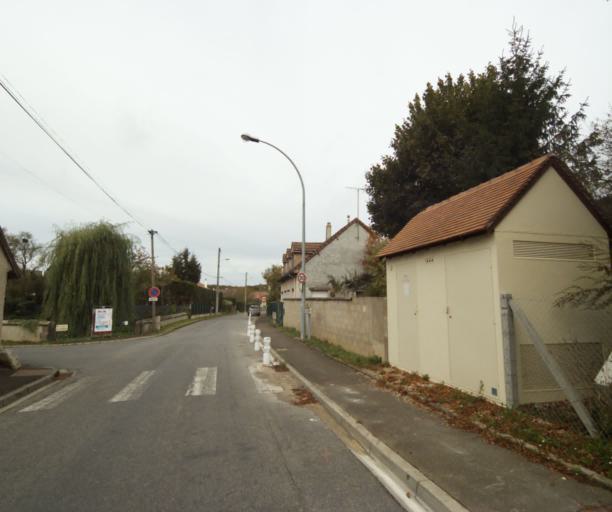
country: FR
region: Centre
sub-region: Departement d'Eure-et-Loir
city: Dreux
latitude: 48.7584
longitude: 1.3566
